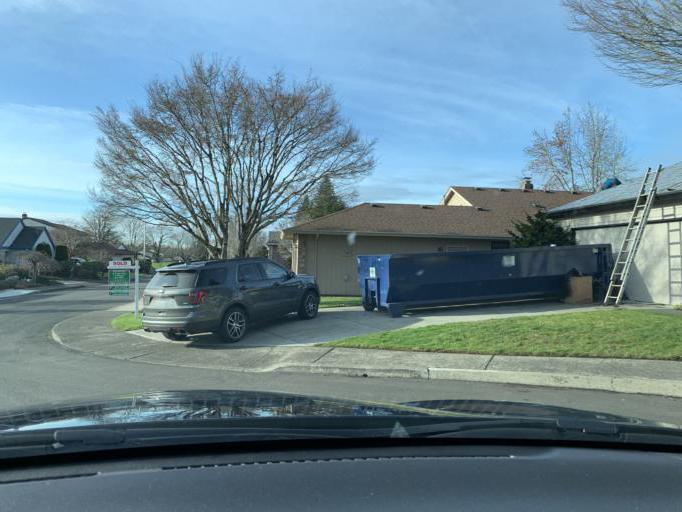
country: US
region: Washington
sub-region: Clark County
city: Mill Plain
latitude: 45.5961
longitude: -122.5109
